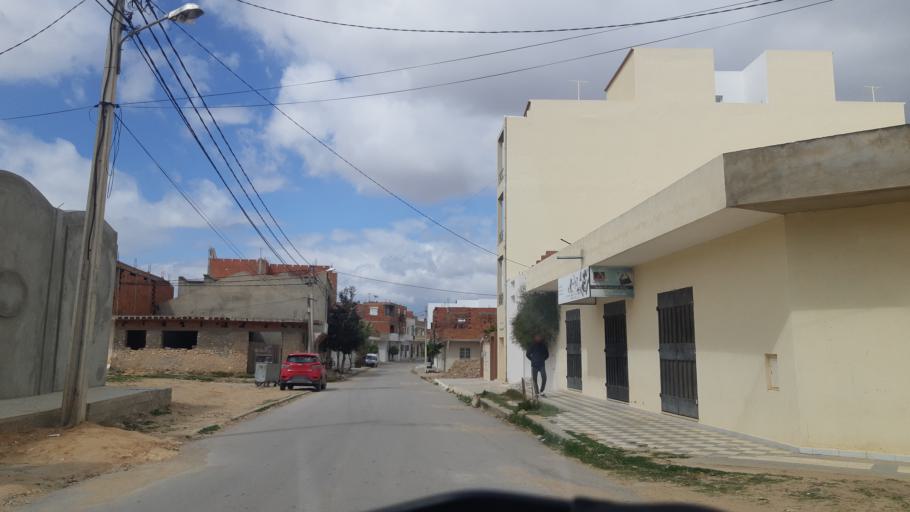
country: TN
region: Susah
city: Akouda
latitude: 35.8641
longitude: 10.5382
